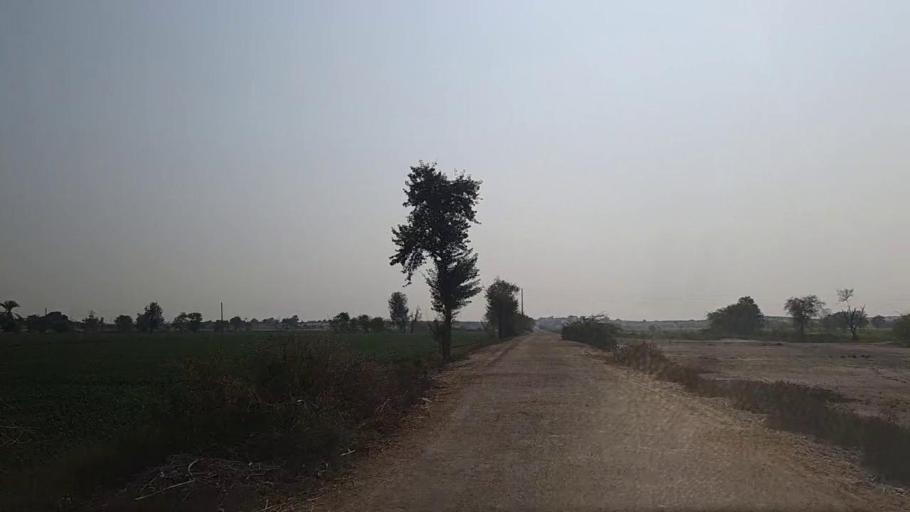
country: PK
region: Sindh
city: Jam Sahib
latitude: 26.4524
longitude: 68.5234
